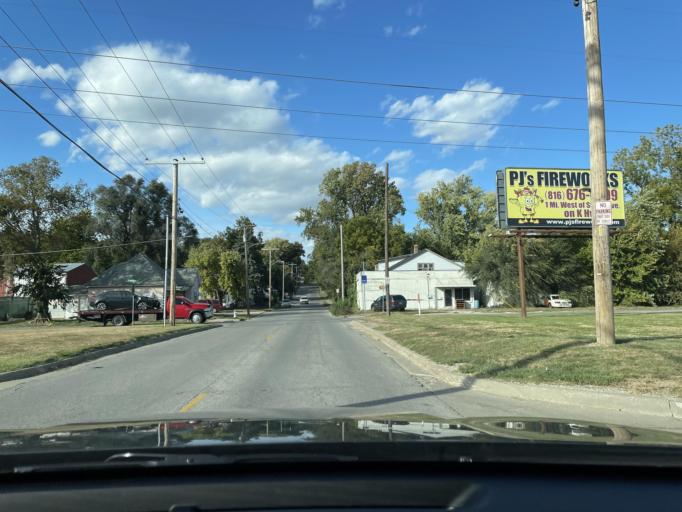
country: US
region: Missouri
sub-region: Buchanan County
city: Saint Joseph
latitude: 39.7380
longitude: -94.8340
